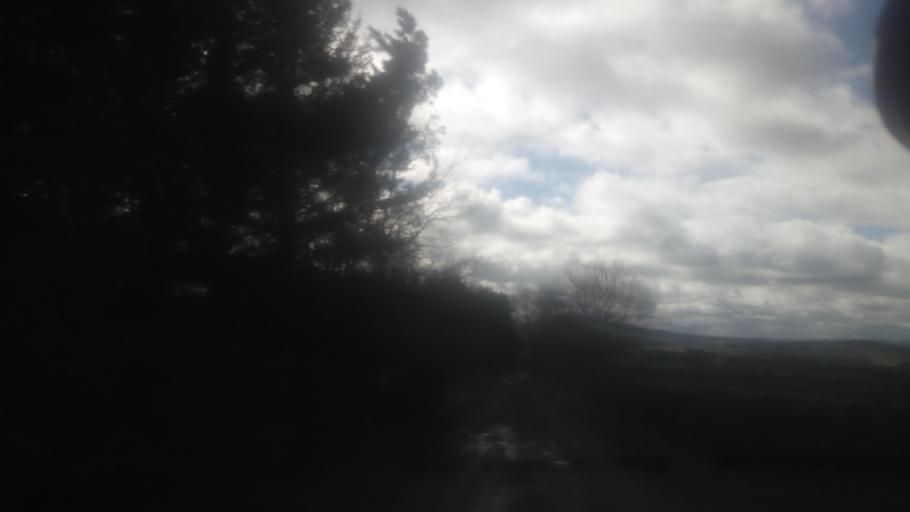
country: GB
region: Scotland
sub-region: The Scottish Borders
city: Jedburgh
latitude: 55.4732
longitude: -2.6063
